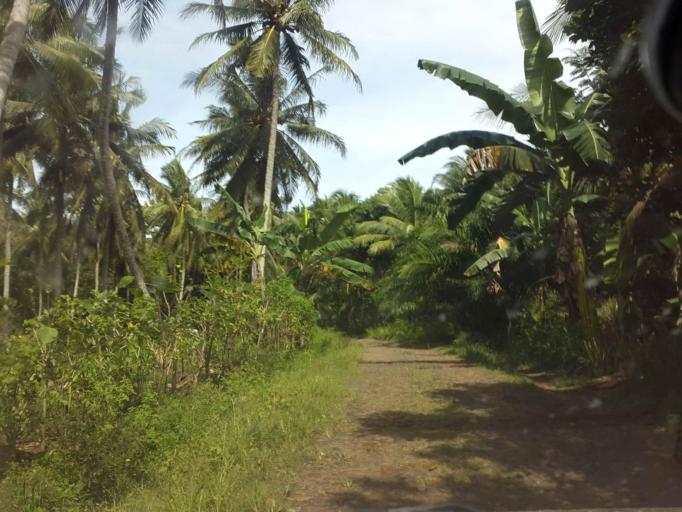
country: ID
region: Lampung
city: Sidorejo
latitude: -5.6309
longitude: 105.4546
